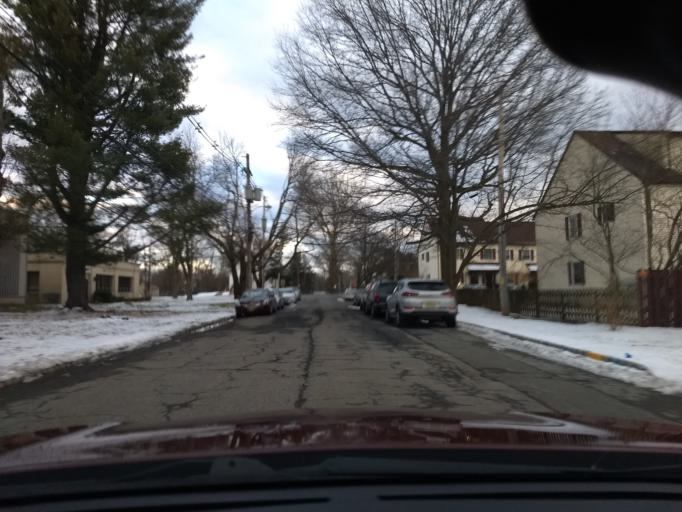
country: US
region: New Jersey
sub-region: Morris County
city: Morris Plains
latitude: 40.8097
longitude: -74.4724
